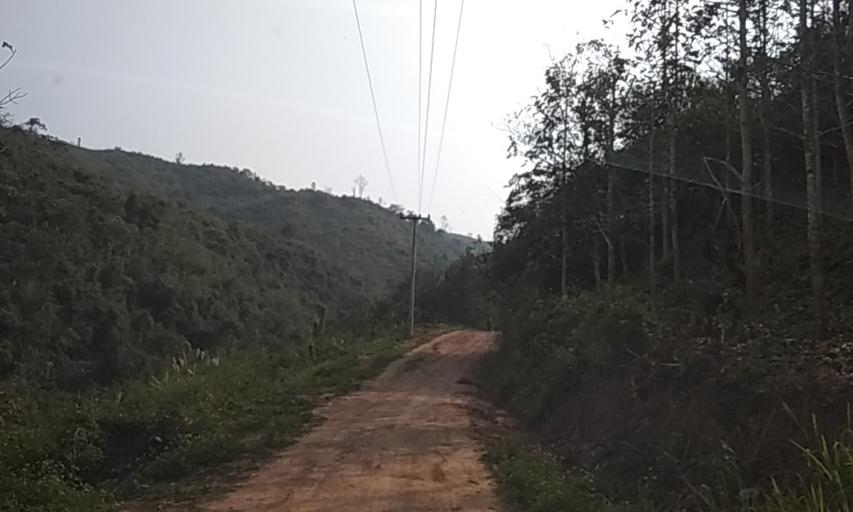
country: LA
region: Louangphabang
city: Louangphabang
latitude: 20.0495
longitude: 101.8492
